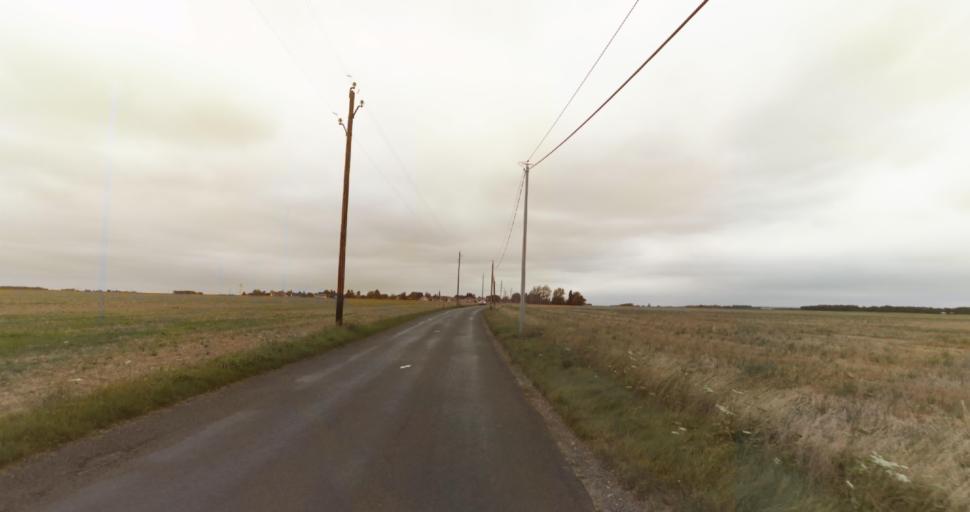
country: FR
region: Haute-Normandie
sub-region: Departement de l'Eure
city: La Couture-Boussey
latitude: 48.9019
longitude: 1.3553
